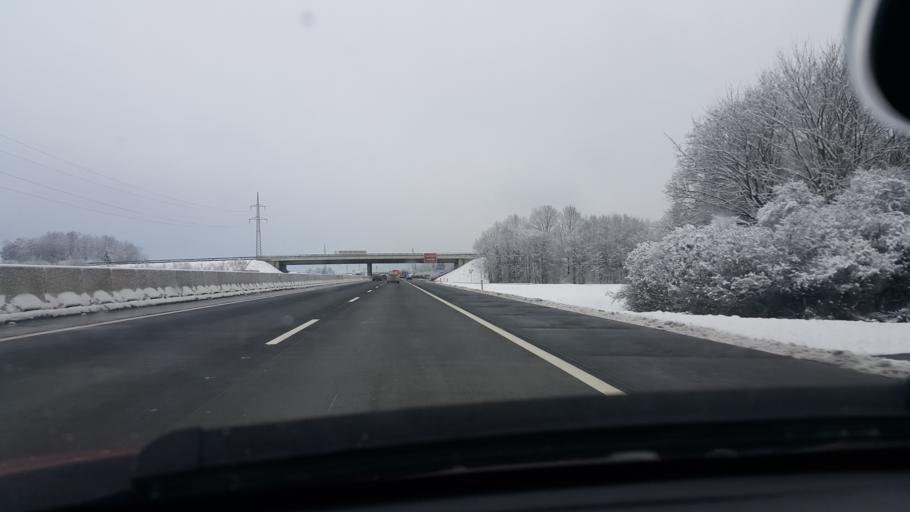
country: AT
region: Styria
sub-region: Politischer Bezirk Graz-Umgebung
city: Zettling
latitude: 46.9613
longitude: 15.4388
